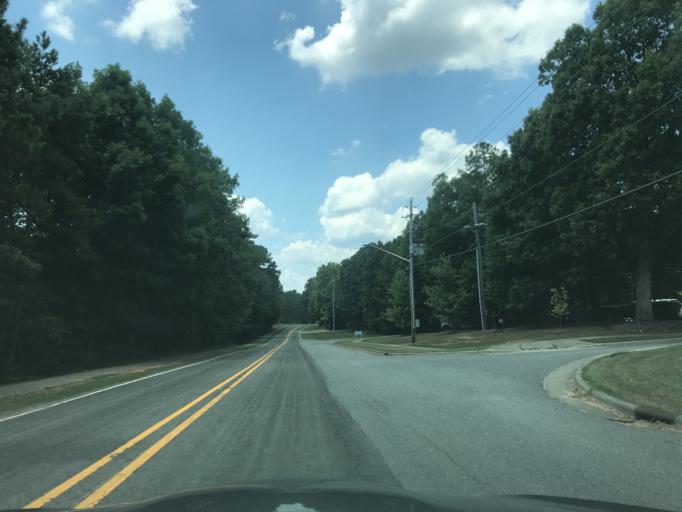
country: US
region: North Carolina
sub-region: Wake County
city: Wake Forest
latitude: 35.9938
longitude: -78.4914
